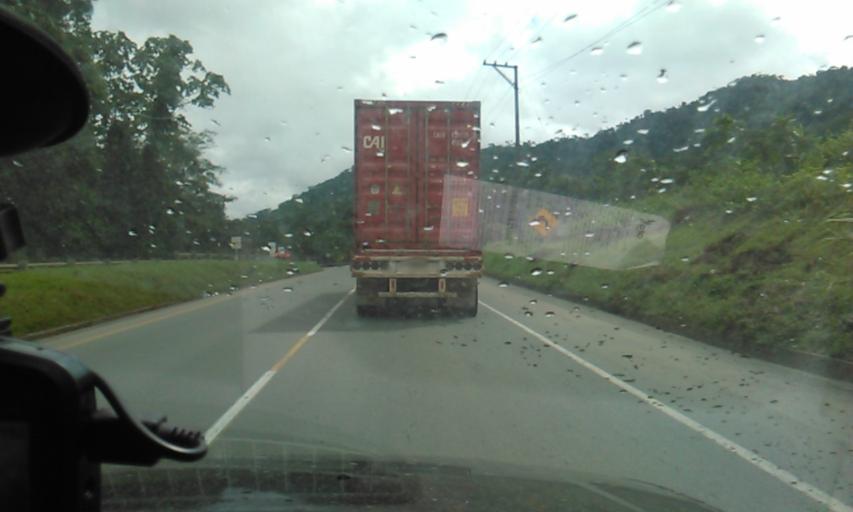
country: CO
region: Valle del Cauca
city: Dagua
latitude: 3.8500
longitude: -76.7983
